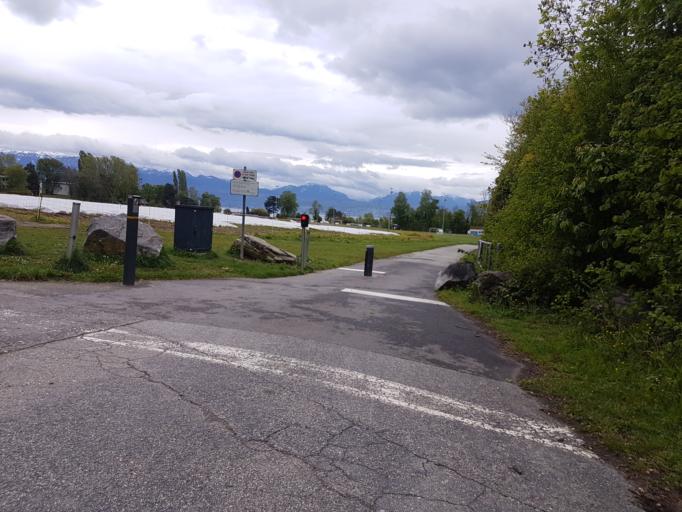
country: CH
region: Vaud
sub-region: Morges District
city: Preverenges
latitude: 46.5115
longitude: 6.5450
